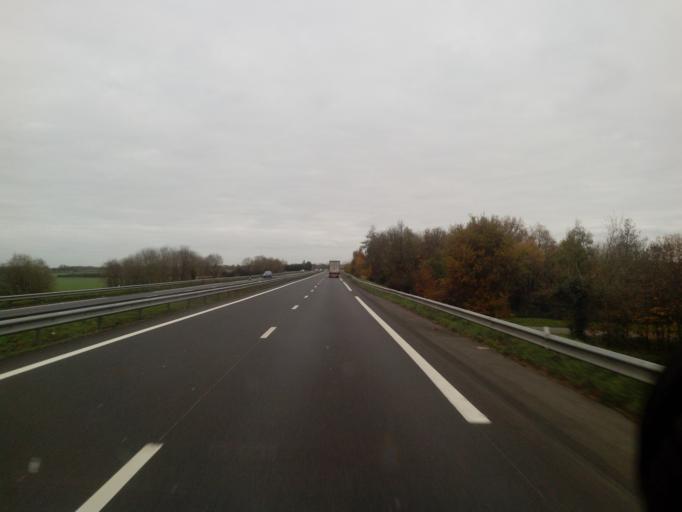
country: FR
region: Pays de la Loire
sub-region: Departement de Maine-et-Loire
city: Roussay
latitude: 47.1095
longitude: -1.0426
